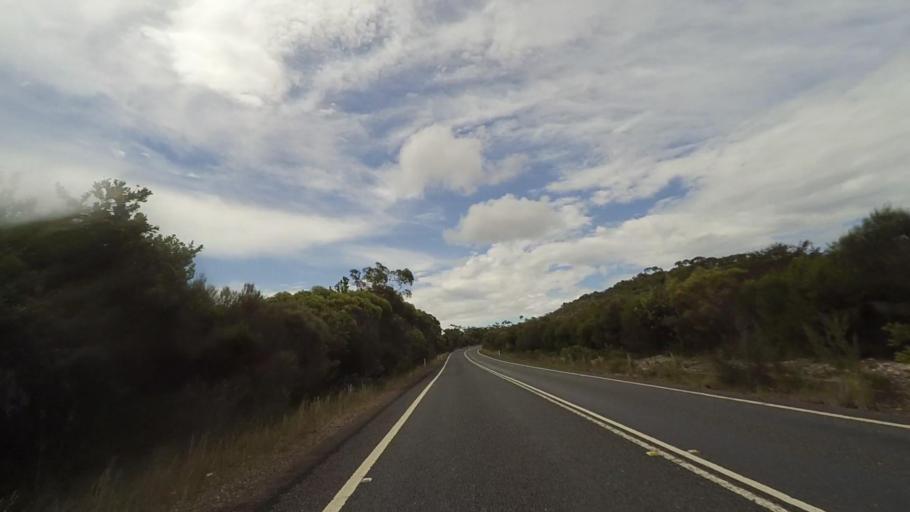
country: AU
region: New South Wales
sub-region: Sutherland Shire
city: Heathcote
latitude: -34.1102
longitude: 151.0597
